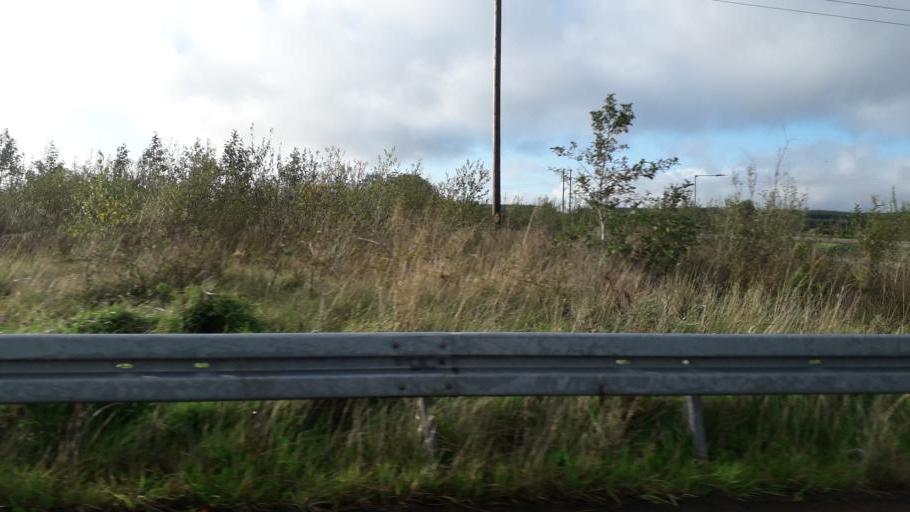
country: IE
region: Connaught
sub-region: Roscommon
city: Ballaghaderreen
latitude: 53.9119
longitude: -8.5555
